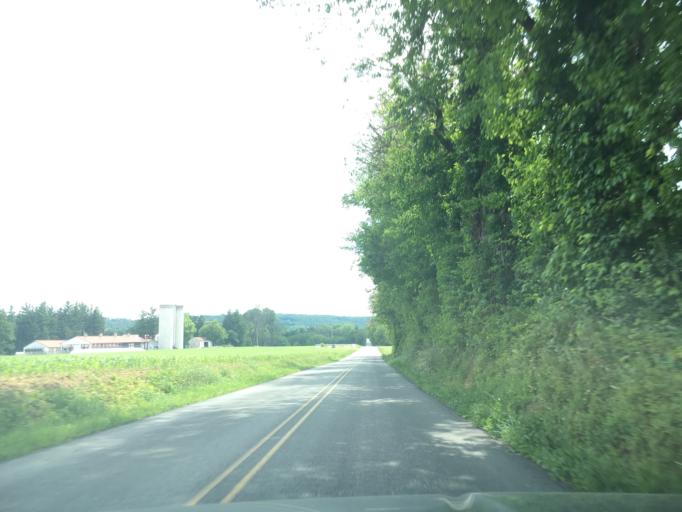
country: US
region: Pennsylvania
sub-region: Berks County
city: Fleetwood
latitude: 40.4660
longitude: -75.8108
